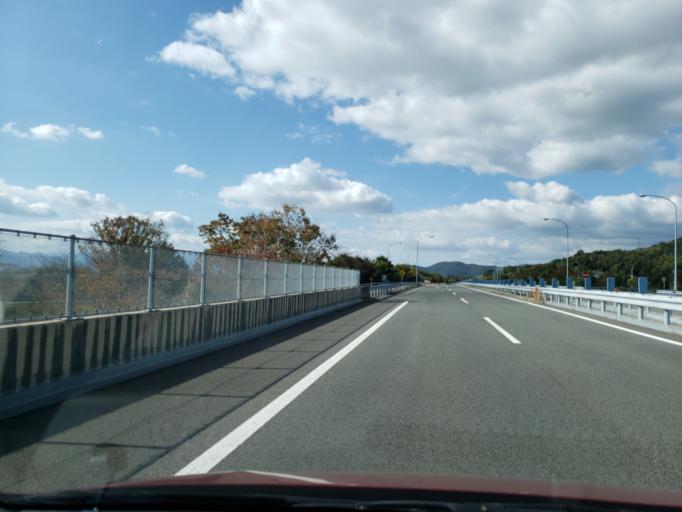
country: JP
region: Tokushima
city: Kamojimacho-jogejima
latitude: 34.1212
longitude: 134.3563
